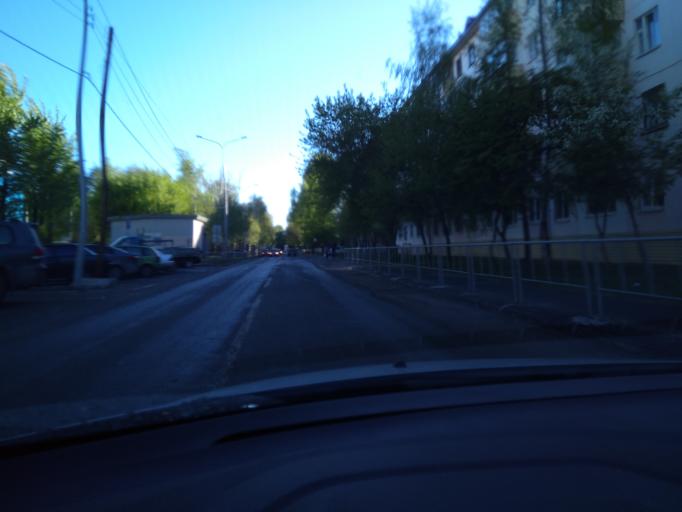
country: RU
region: Tjumen
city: Tyumen
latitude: 57.1337
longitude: 65.5919
